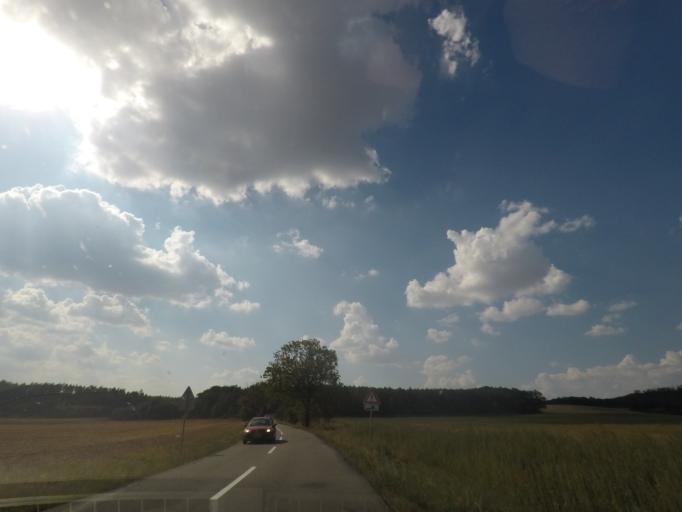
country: CZ
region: Kralovehradecky
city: Trebechovice pod Orebem
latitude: 50.2190
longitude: 15.9805
